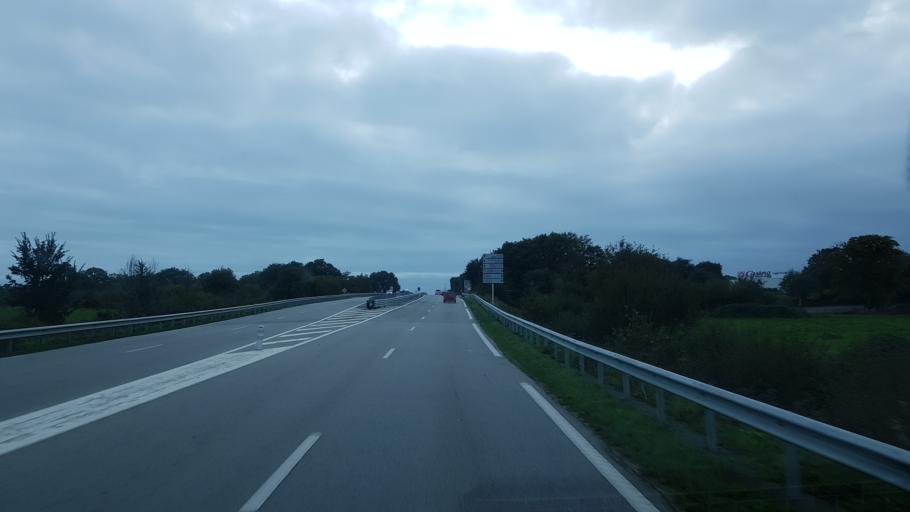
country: FR
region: Brittany
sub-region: Departement du Morbihan
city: Sarzeau
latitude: 47.5296
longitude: -2.7513
